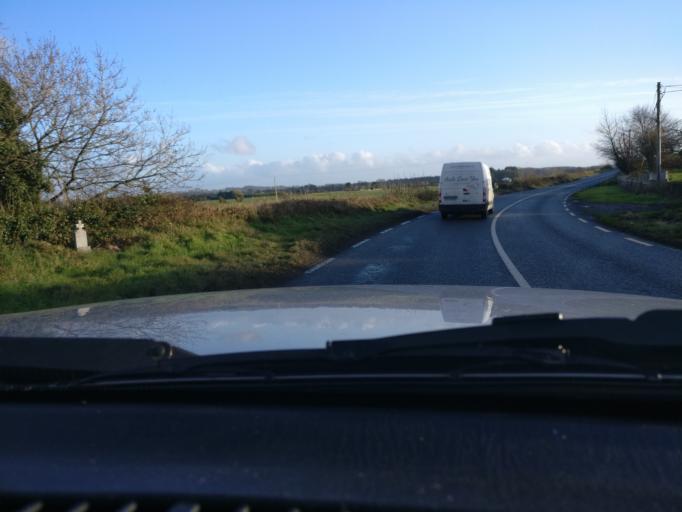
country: IE
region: Ulster
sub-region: An Cabhan
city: Mullagh
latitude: 53.7250
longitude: -6.9841
